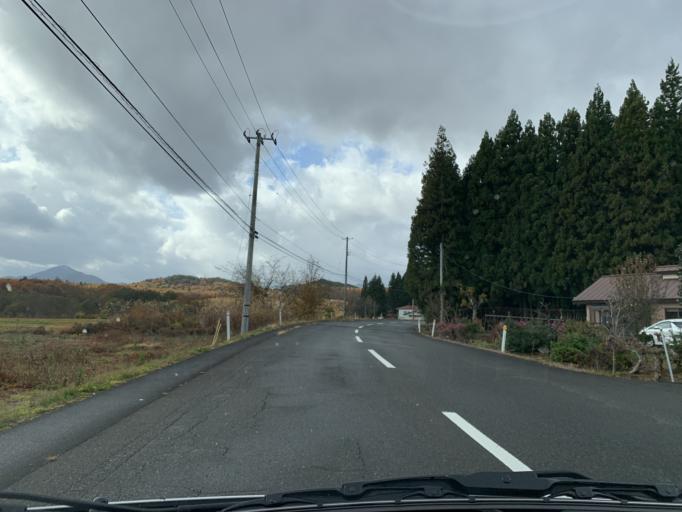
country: JP
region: Iwate
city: Mizusawa
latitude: 39.1098
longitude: 140.9689
